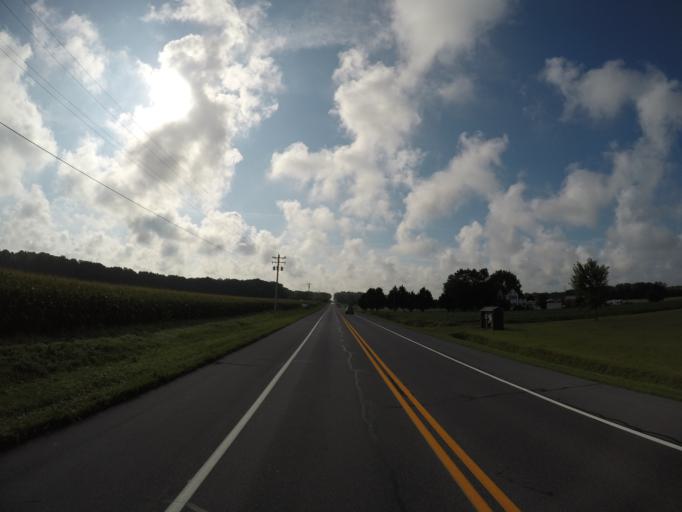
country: US
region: Delaware
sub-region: Sussex County
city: Bridgeville
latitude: 38.7683
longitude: -75.6495
